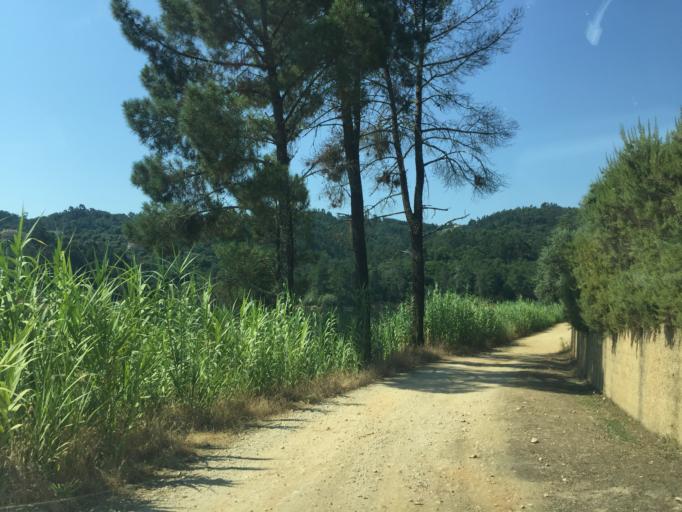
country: PT
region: Santarem
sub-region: Ferreira do Zezere
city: Ferreira do Zezere
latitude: 39.6057
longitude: -8.2762
